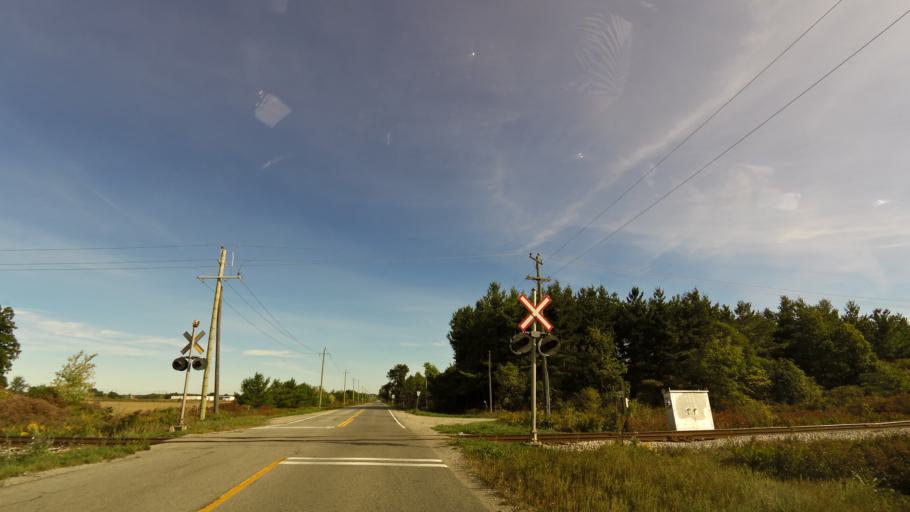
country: CA
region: Ontario
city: Ancaster
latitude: 43.0292
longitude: -80.0103
